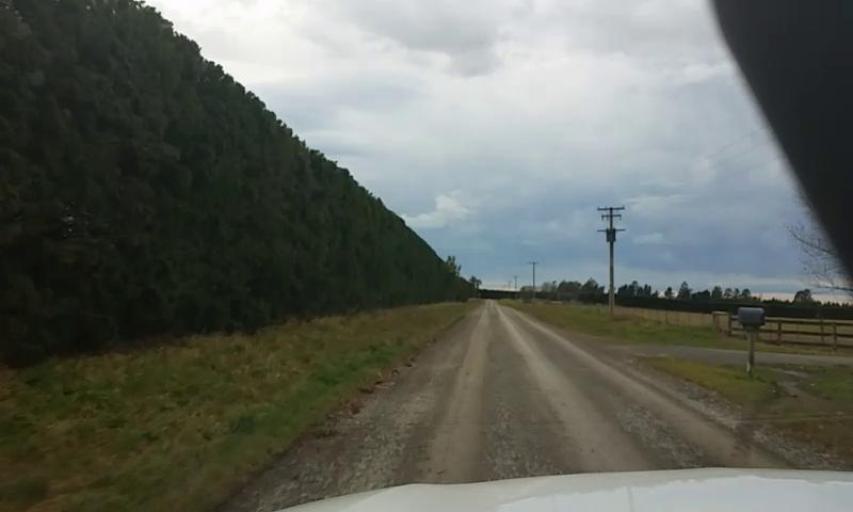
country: NZ
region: Canterbury
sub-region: Waimakariri District
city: Kaiapoi
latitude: -43.2909
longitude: 172.4402
